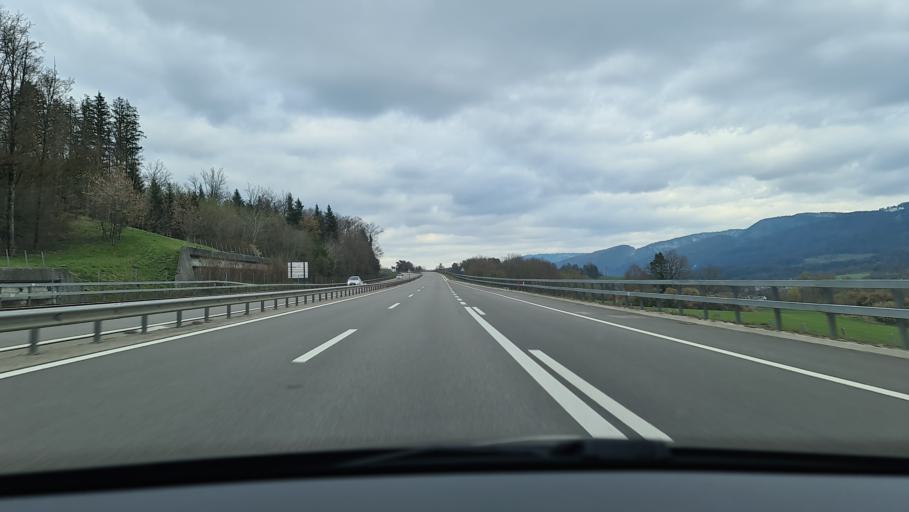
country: CH
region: Jura
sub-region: Delemont District
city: Bassecourt
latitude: 47.3452
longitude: 7.2638
